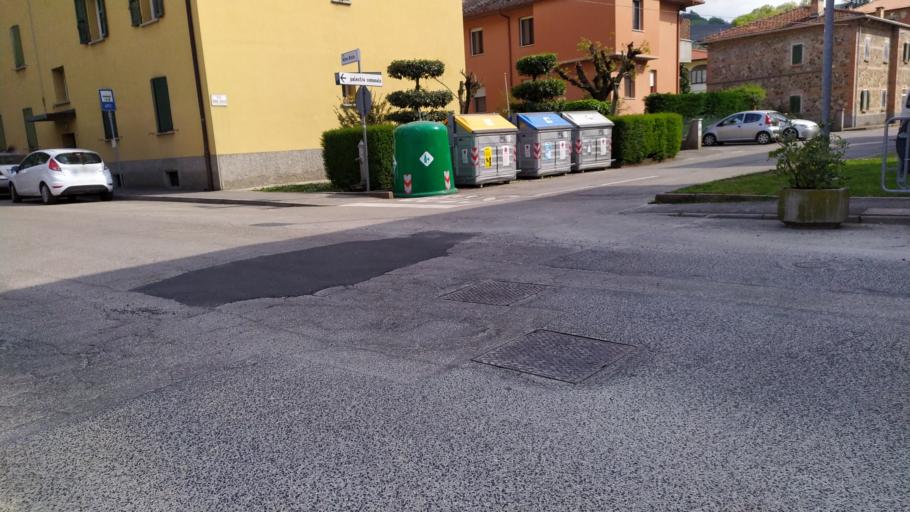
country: IT
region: Emilia-Romagna
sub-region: Provincia di Bologna
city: Borgo Tossignano
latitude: 44.2769
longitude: 11.5901
